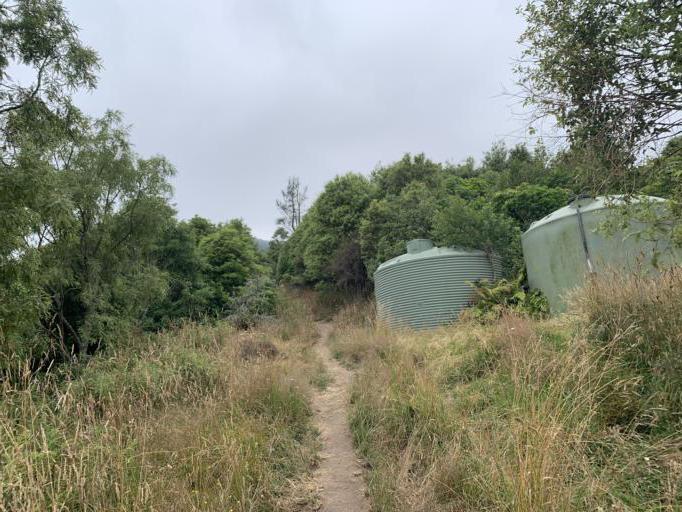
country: NZ
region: Waikato
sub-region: Taupo District
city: Taupo
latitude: -38.6982
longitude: 176.1459
